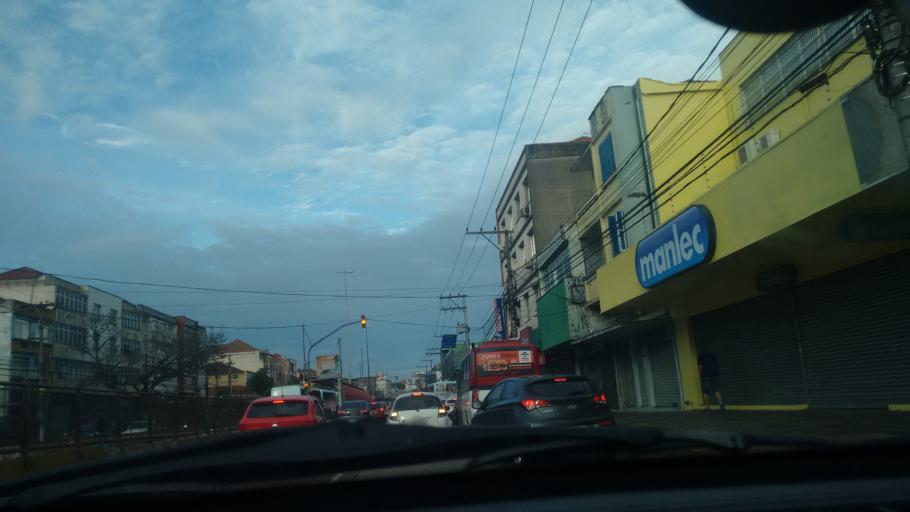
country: BR
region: Rio Grande do Sul
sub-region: Porto Alegre
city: Porto Alegre
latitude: -30.0112
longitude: -51.1640
